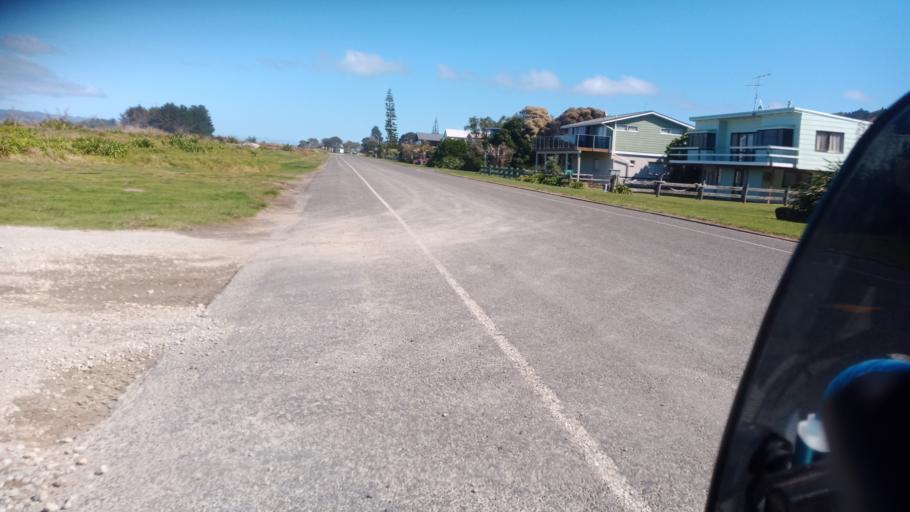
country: NZ
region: Gisborne
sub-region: Gisborne District
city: Gisborne
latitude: -39.0149
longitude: 177.8860
